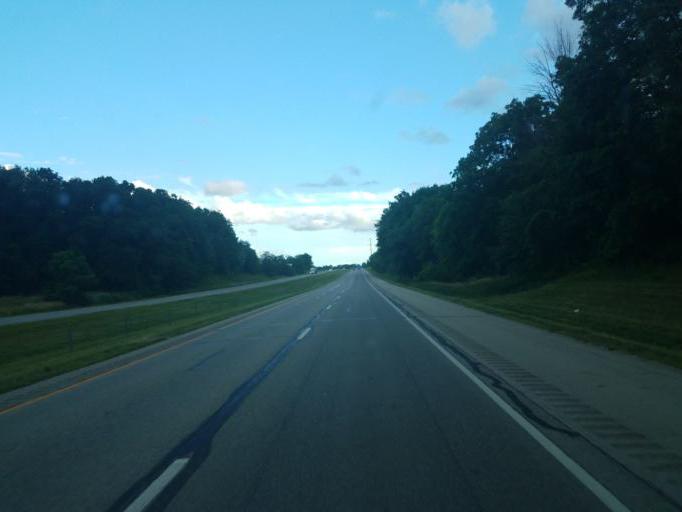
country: US
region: Indiana
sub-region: DeKalb County
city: Garrett
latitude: 41.2738
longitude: -85.0872
